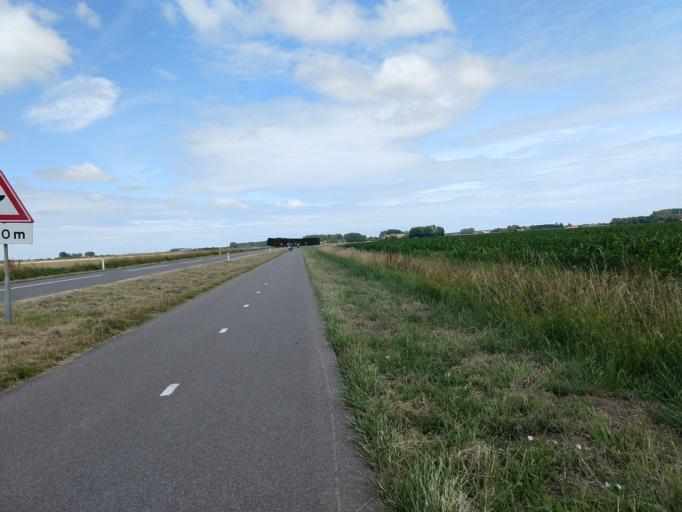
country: NL
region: Zeeland
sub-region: Gemeente Goes
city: Goes
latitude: 51.5132
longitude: 3.8291
